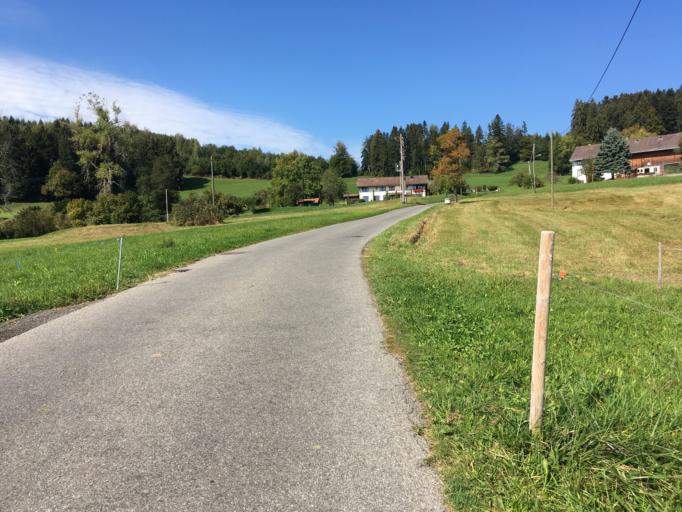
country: CH
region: Zurich
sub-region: Bezirk Hinwil
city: Baretswil
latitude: 47.3429
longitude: 8.8429
